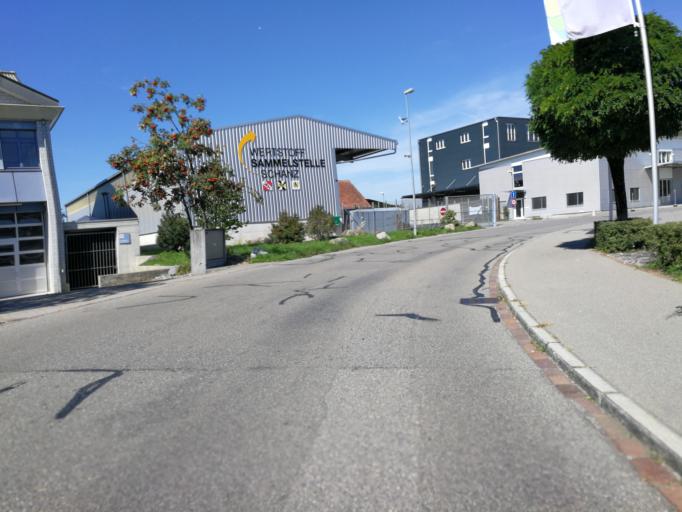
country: CH
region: Zurich
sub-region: Bezirk Pfaeffikon
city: Pfaeffikon / Pfaeffikon (Dorfkern)
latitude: 47.3649
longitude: 8.7687
